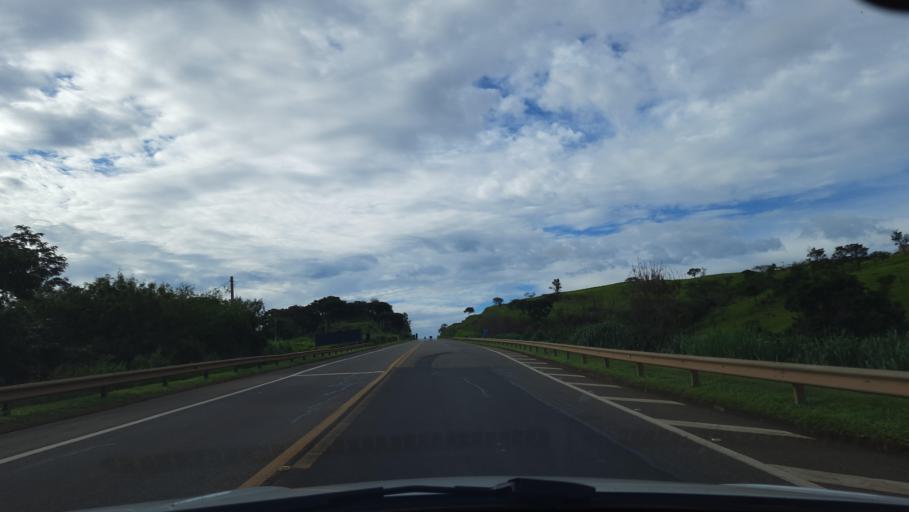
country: BR
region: Sao Paulo
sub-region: Sao Joao Da Boa Vista
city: Sao Joao da Boa Vista
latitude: -21.9728
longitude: -46.8257
